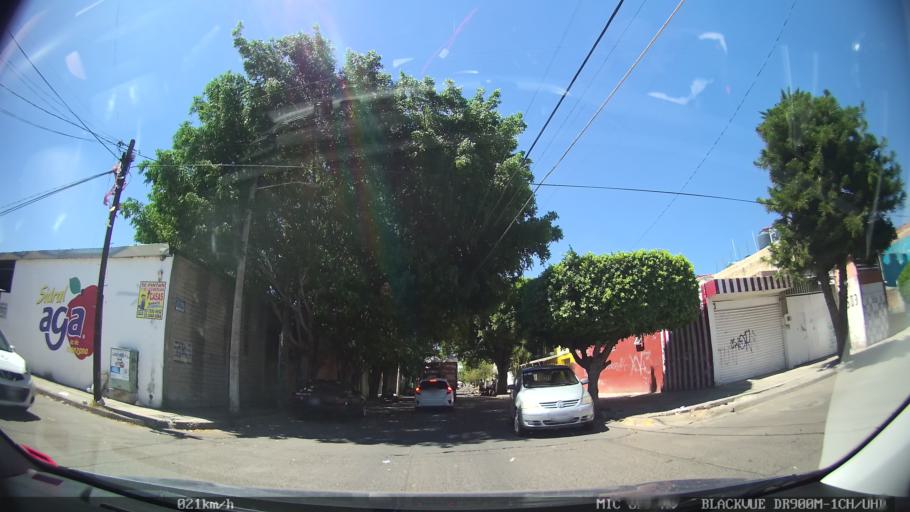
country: MX
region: Jalisco
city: Tlaquepaque
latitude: 20.6636
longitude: -103.2853
